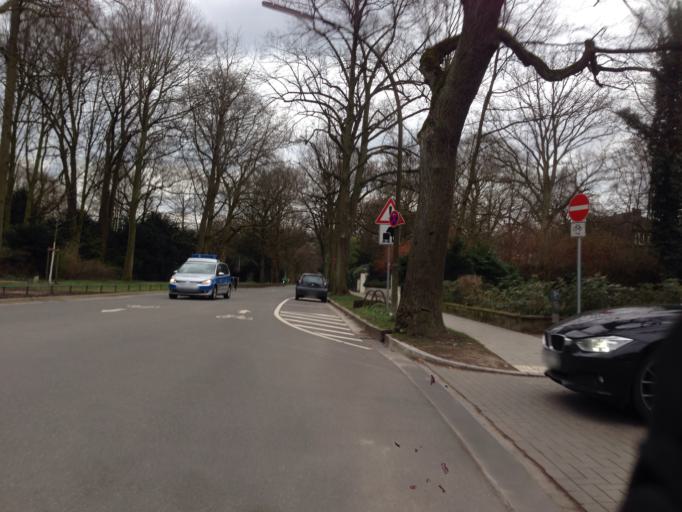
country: DE
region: Hamburg
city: Hamburg
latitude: 53.5733
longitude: 9.9994
